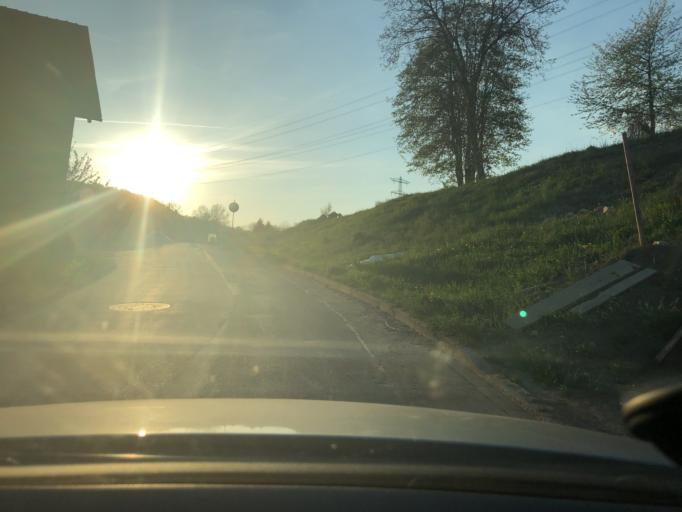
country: DE
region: Baden-Wuerttemberg
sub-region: Freiburg Region
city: Waldshut-Tiengen
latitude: 47.6549
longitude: 8.1938
